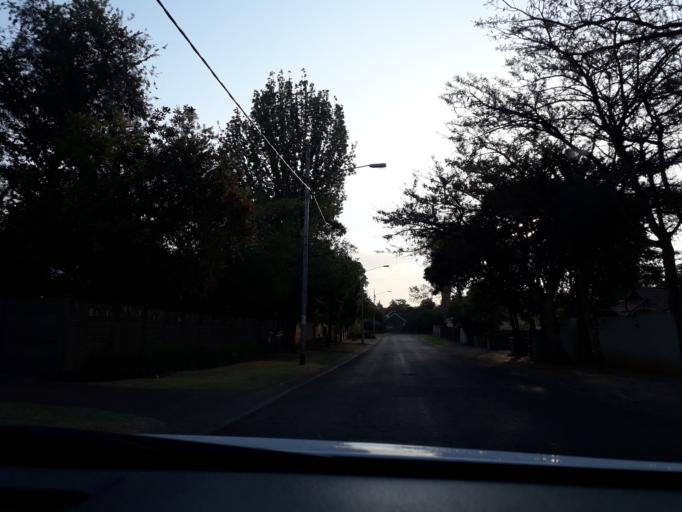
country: ZA
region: Gauteng
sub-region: City of Tshwane Metropolitan Municipality
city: Centurion
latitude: -25.8606
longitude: 28.2108
